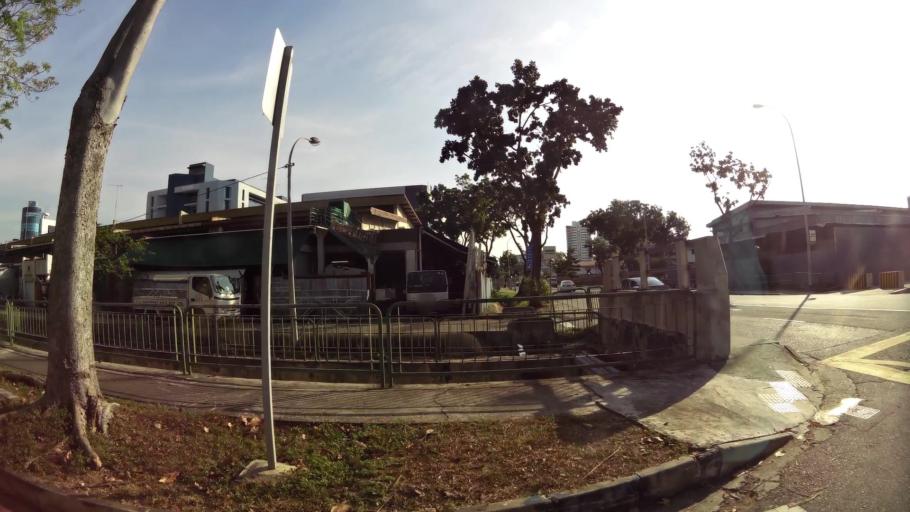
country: SG
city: Singapore
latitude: 1.3229
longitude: 103.8778
